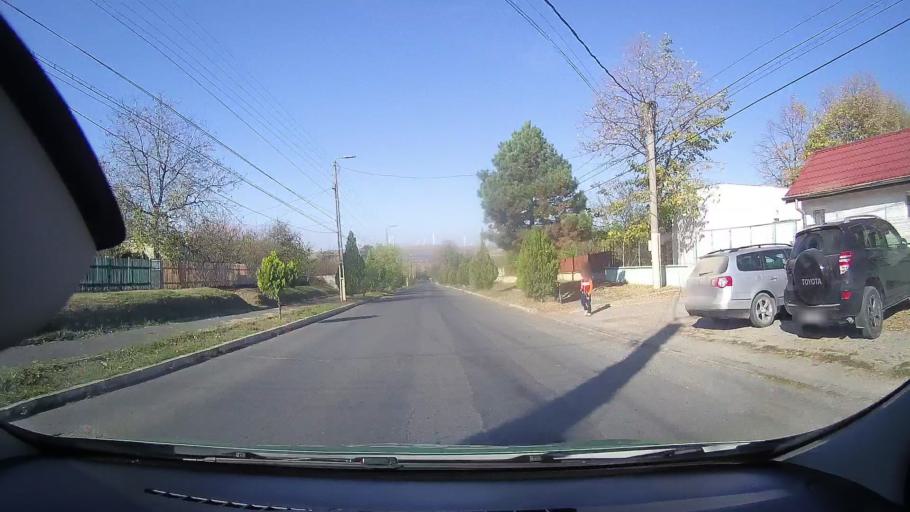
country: RO
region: Tulcea
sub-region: Oras Babadag
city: Babadag
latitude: 44.8880
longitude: 28.7321
